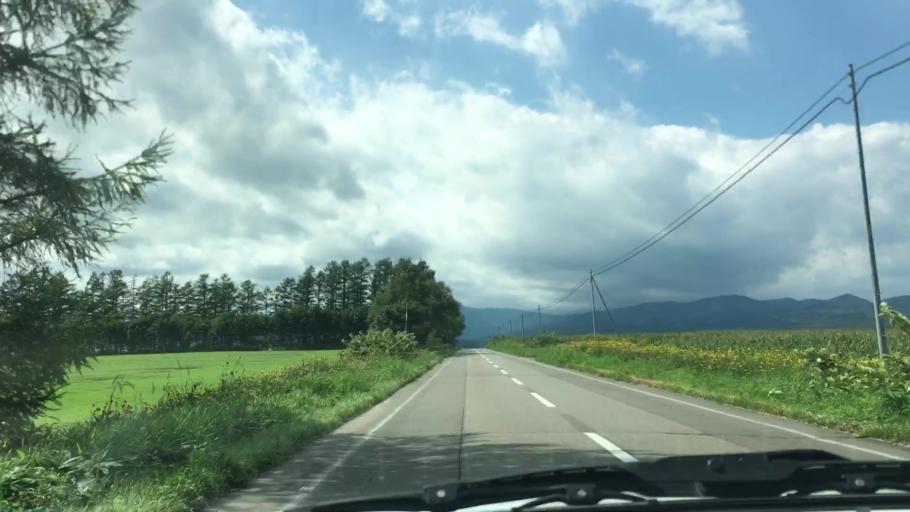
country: JP
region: Hokkaido
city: Otofuke
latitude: 43.2793
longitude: 143.3480
